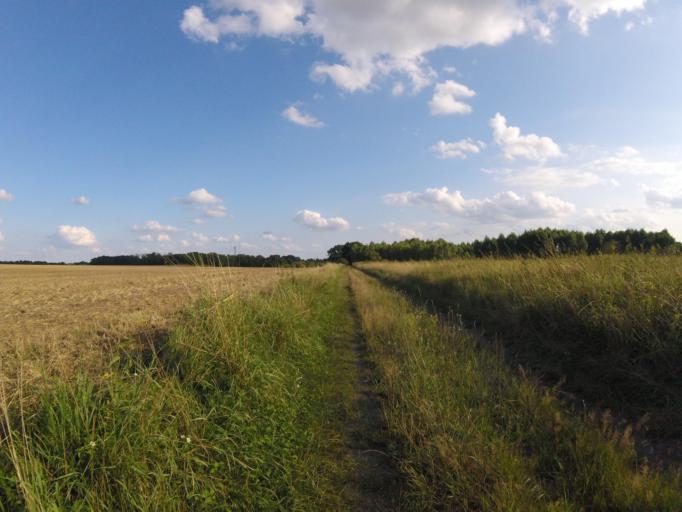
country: DE
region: Brandenburg
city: Mittenwalde
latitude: 52.2987
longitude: 13.5451
